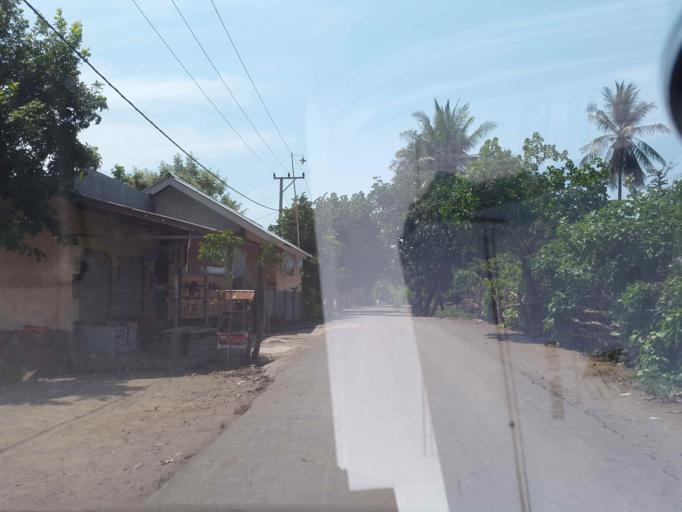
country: ID
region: West Nusa Tenggara
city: Karangkebon Timur
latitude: -8.6747
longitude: 116.0740
